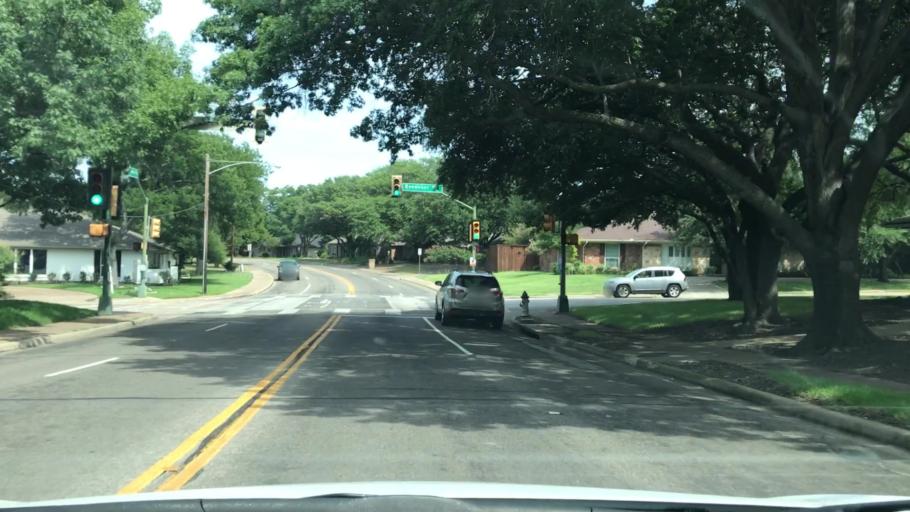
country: US
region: Texas
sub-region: Dallas County
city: University Park
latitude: 32.8867
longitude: -96.7777
